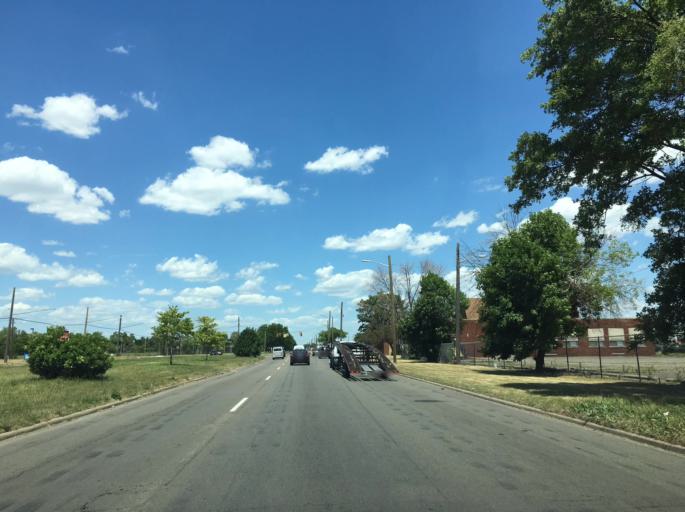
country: US
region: Michigan
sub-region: Macomb County
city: Warren
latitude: 42.4394
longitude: -83.0436
